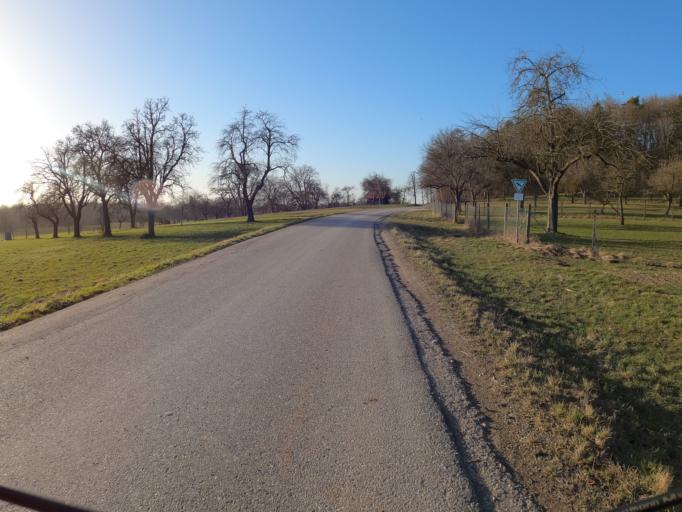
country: DE
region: Bavaria
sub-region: Swabia
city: Holzheim
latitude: 48.4056
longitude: 10.0985
